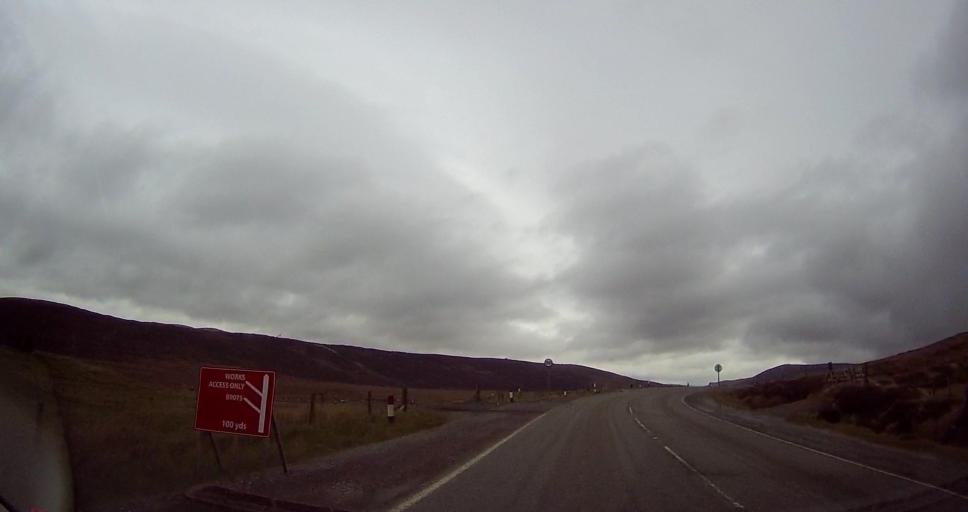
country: GB
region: Scotland
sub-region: Shetland Islands
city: Lerwick
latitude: 60.2779
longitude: -1.2445
